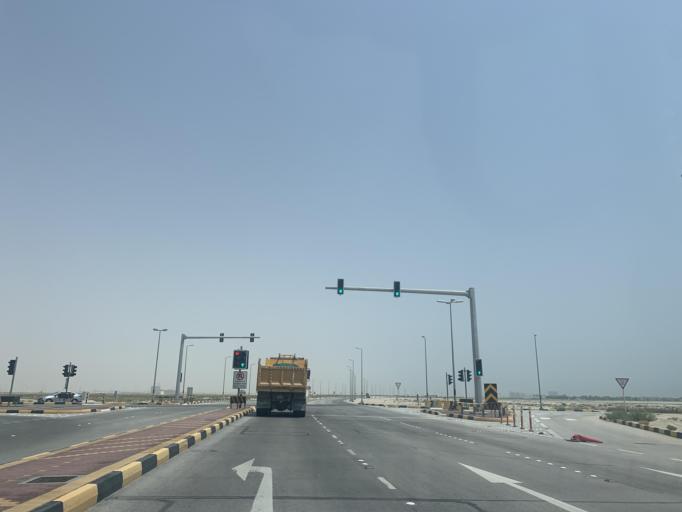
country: BH
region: Central Governorate
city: Dar Kulayb
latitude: 25.8383
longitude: 50.5919
